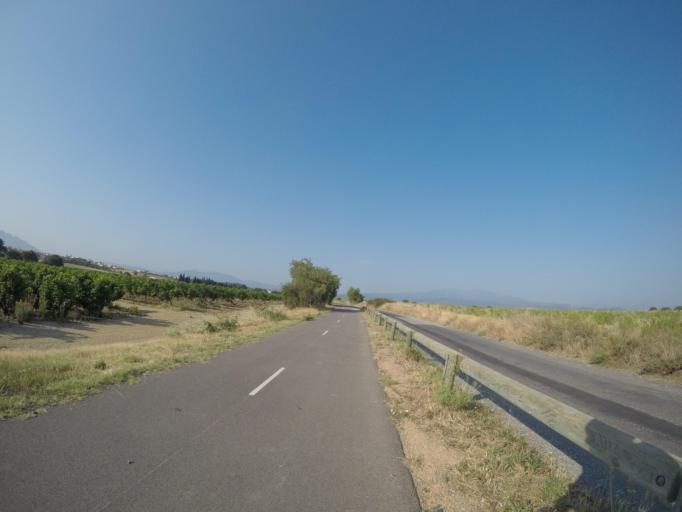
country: FR
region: Languedoc-Roussillon
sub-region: Departement des Pyrenees-Orientales
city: Ponteilla
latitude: 42.6369
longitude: 2.8102
